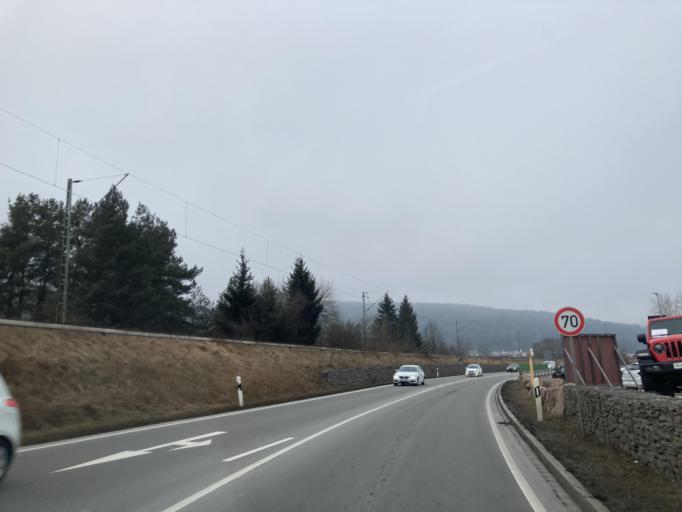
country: DE
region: Baden-Wuerttemberg
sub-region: Freiburg Region
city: Wurmlingen
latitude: 47.9657
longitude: 8.7844
